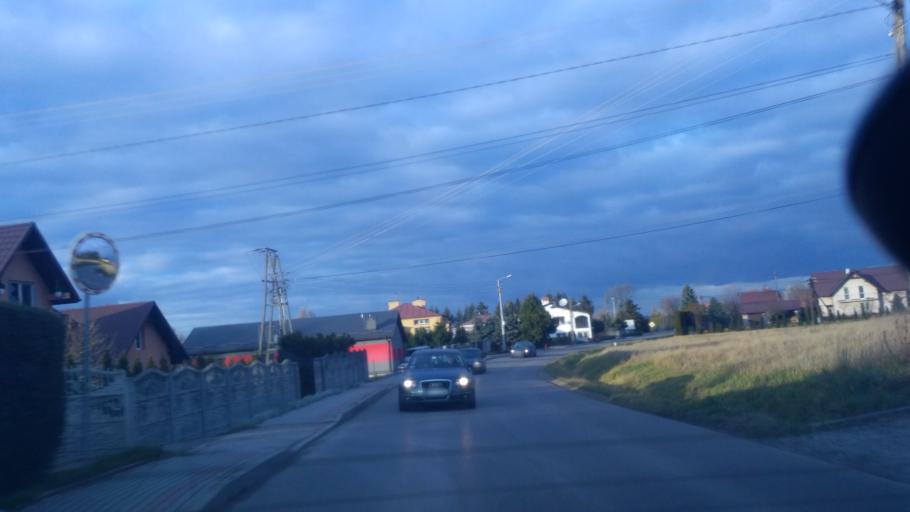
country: PL
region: Subcarpathian Voivodeship
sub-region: Powiat rzeszowski
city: Krasne
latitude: 50.0567
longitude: 22.1200
